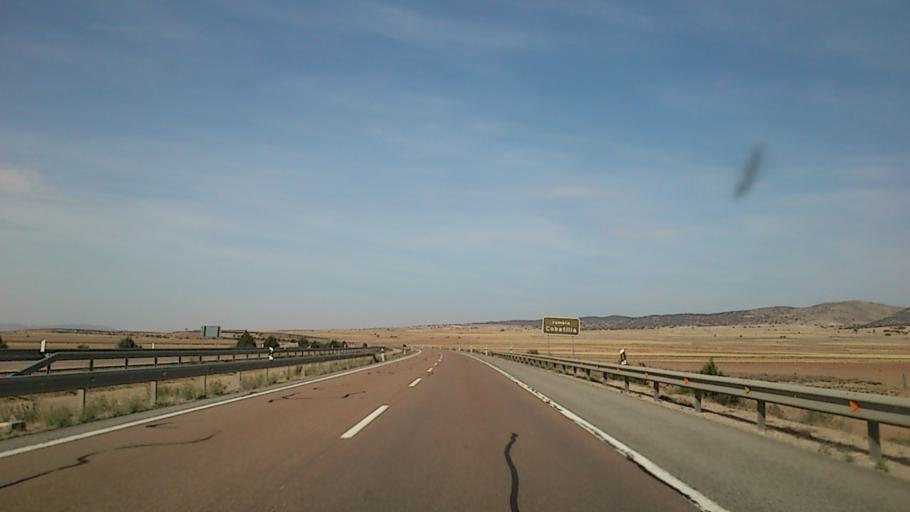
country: ES
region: Aragon
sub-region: Provincia de Teruel
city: Singra
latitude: 40.6672
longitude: -1.3150
